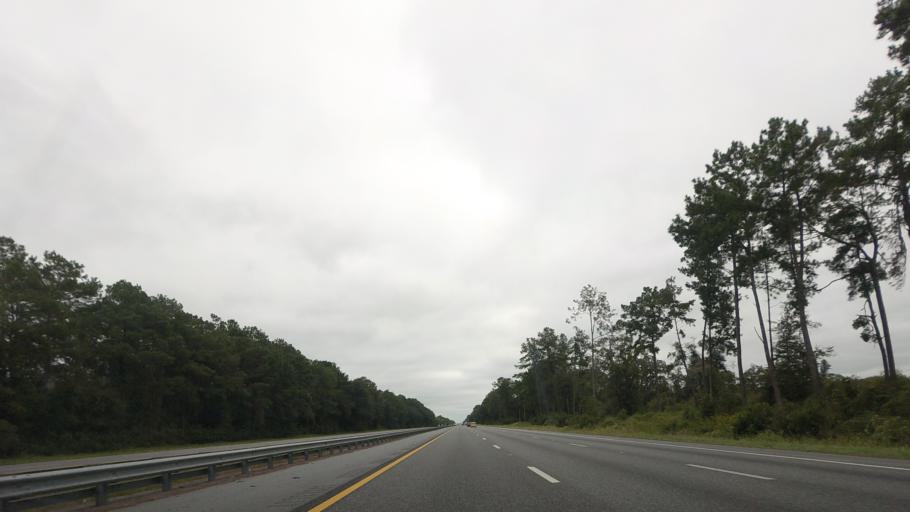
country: US
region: Florida
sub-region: Hamilton County
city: Jasper
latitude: 30.4702
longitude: -82.9686
